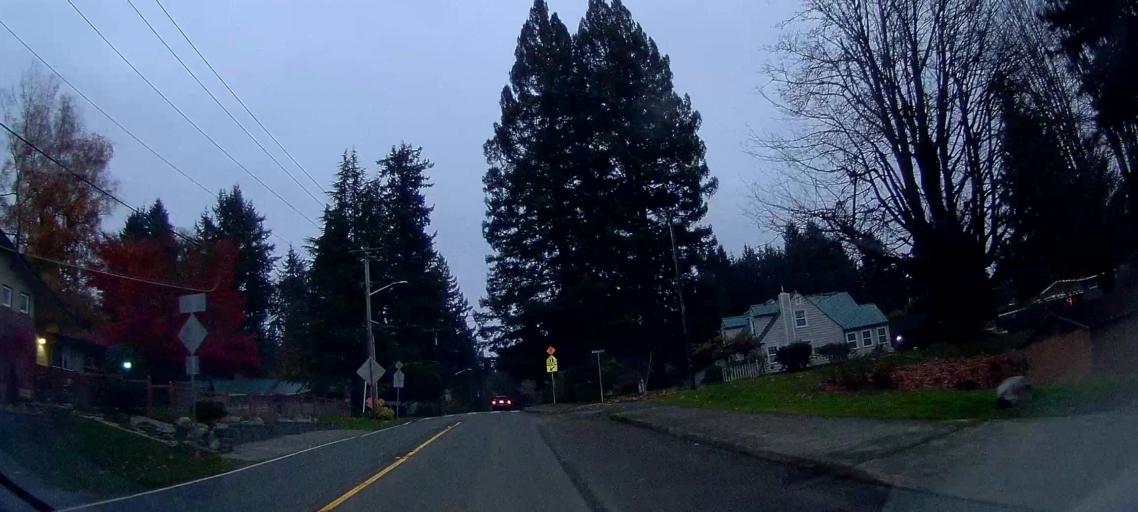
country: US
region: Washington
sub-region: Thurston County
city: Olympia
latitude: 47.0232
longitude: -122.8773
